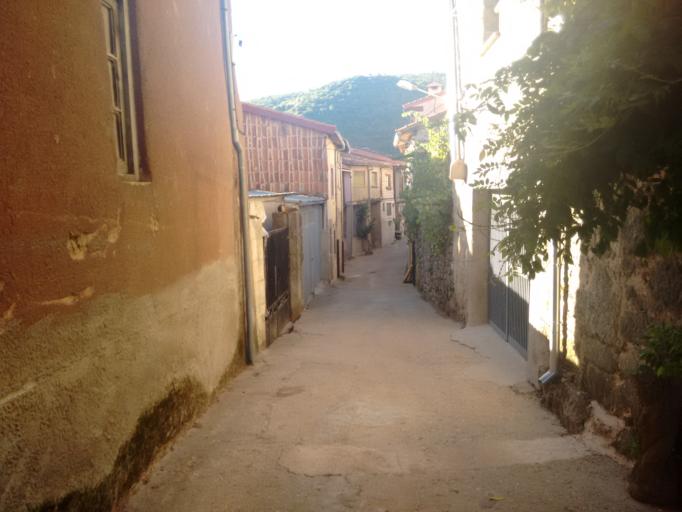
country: ES
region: Castille and Leon
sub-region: Provincia de Salamanca
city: San Esteban de la Sierra
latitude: 40.5067
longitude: -5.9078
